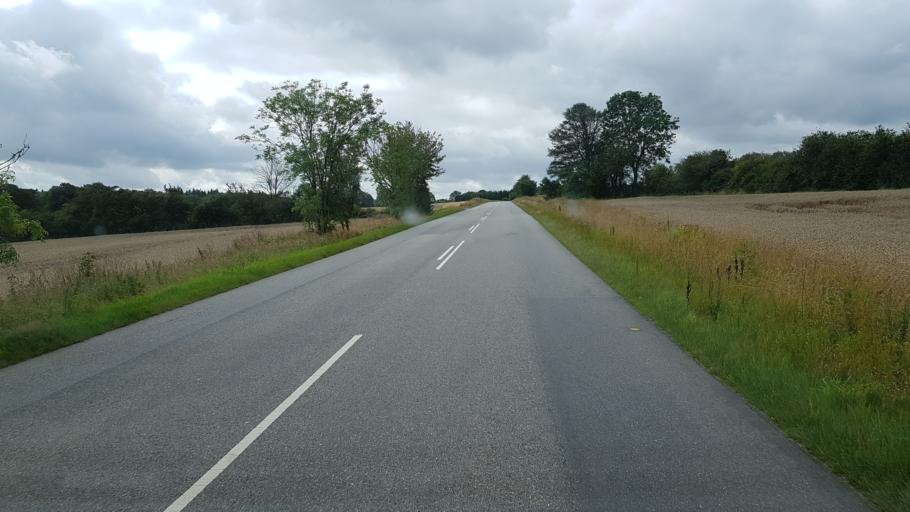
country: DK
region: South Denmark
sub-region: Kolding Kommune
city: Kolding
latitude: 55.4748
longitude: 9.4041
